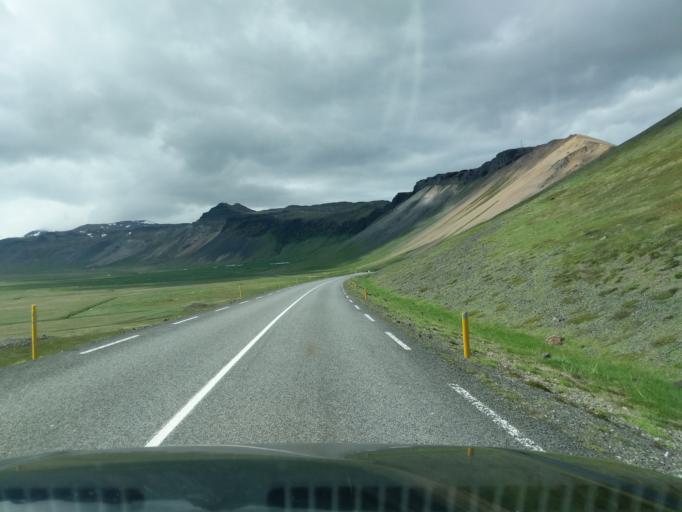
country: IS
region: West
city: Olafsvik
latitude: 64.8247
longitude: -23.4474
